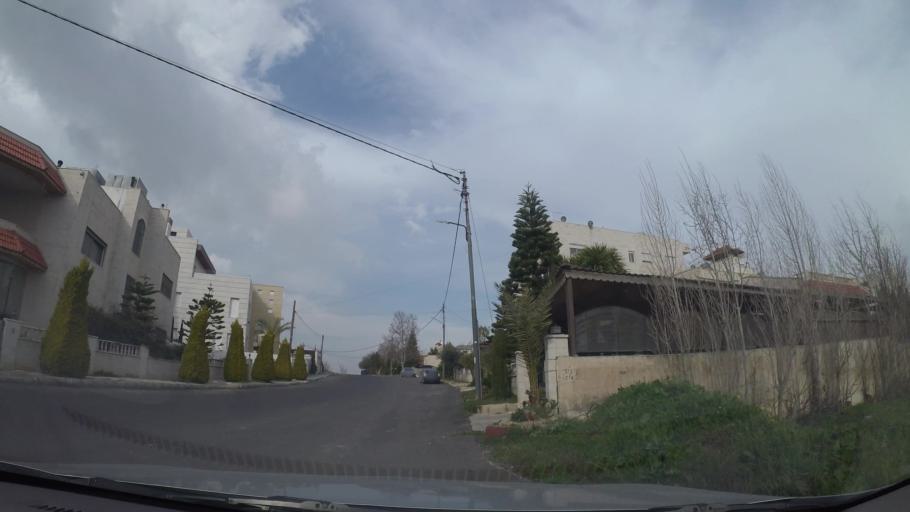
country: JO
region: Amman
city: Umm as Summaq
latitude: 31.8869
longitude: 35.8667
